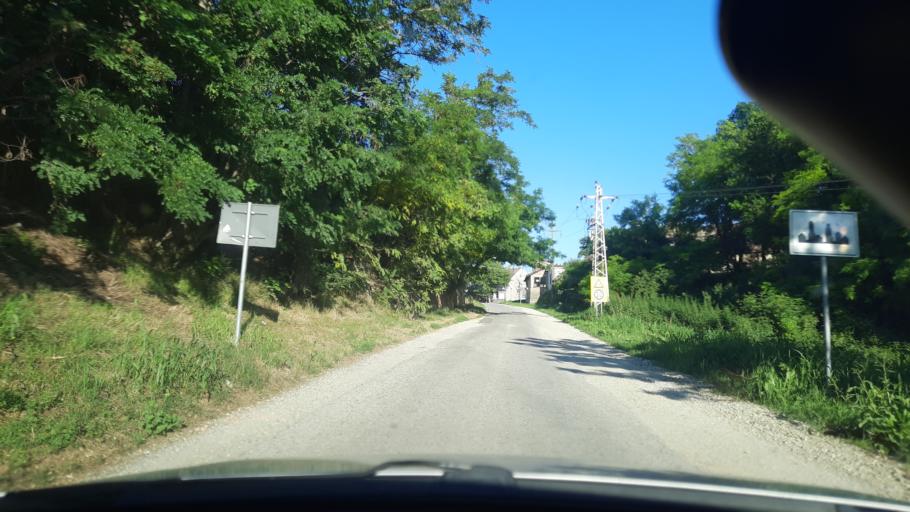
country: RS
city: Cortanovci
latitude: 45.1019
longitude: 19.9904
